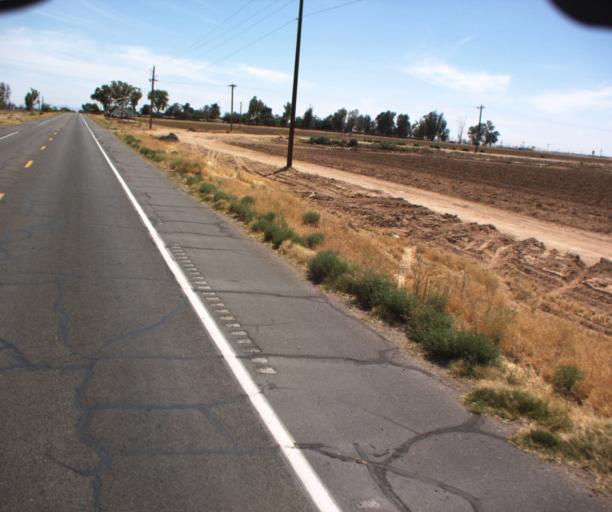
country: US
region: Arizona
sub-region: Pinal County
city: Coolidge
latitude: 32.9130
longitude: -111.5151
